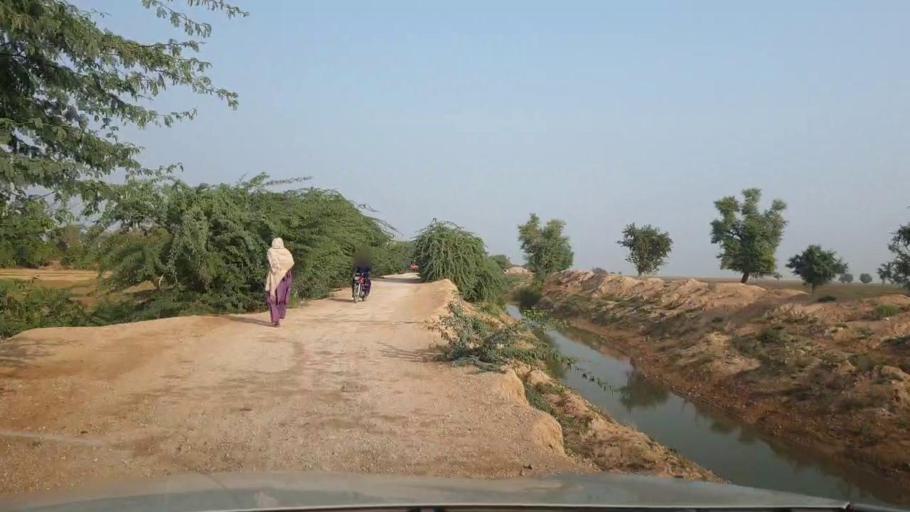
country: PK
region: Sindh
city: Sehwan
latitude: 26.3458
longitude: 67.7237
